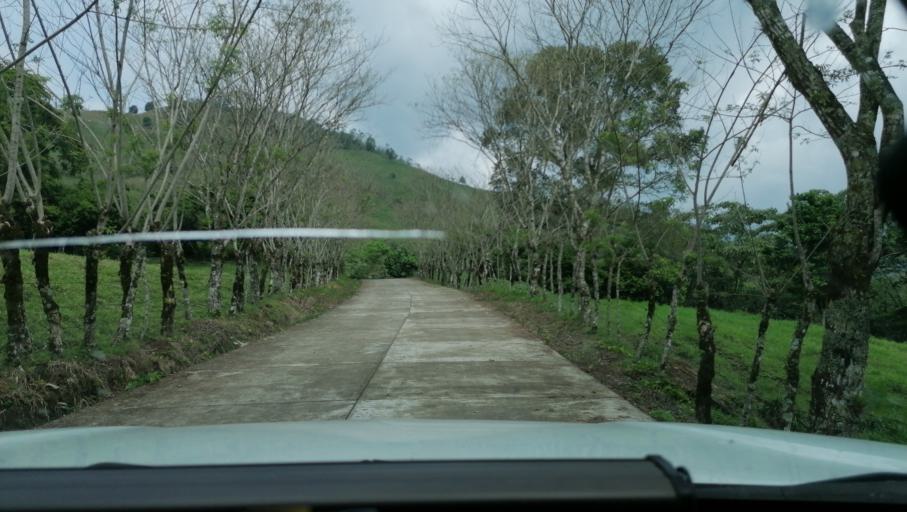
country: MX
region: Chiapas
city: Ocotepec
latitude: 17.3258
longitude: -93.1696
